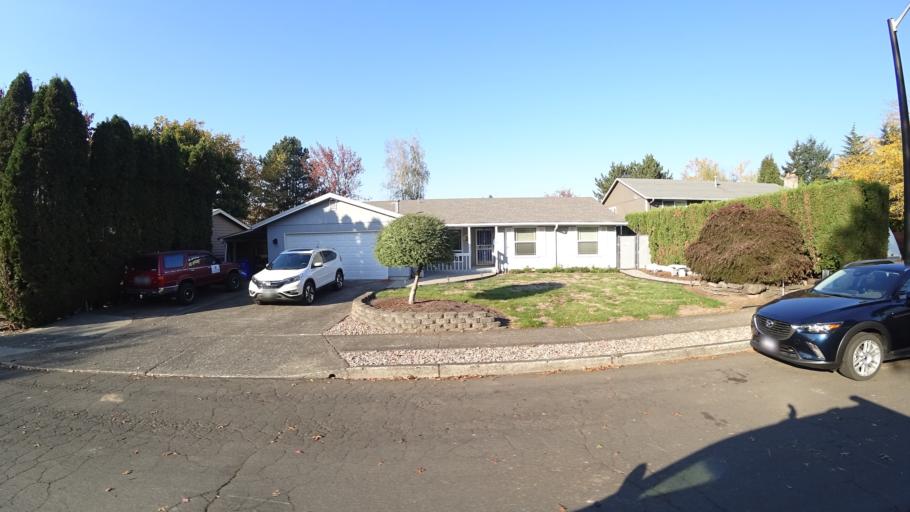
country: US
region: Oregon
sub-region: Multnomah County
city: Gresham
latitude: 45.5078
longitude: -122.4536
